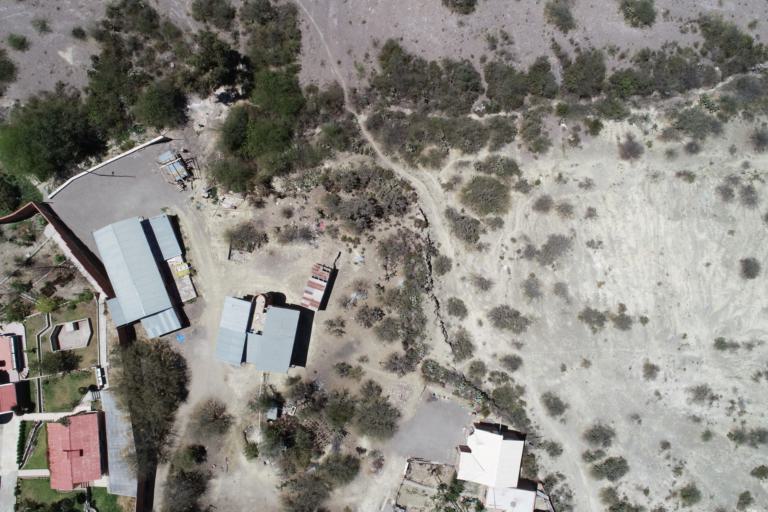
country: BO
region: La Paz
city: La Paz
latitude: -16.6470
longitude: -68.0417
